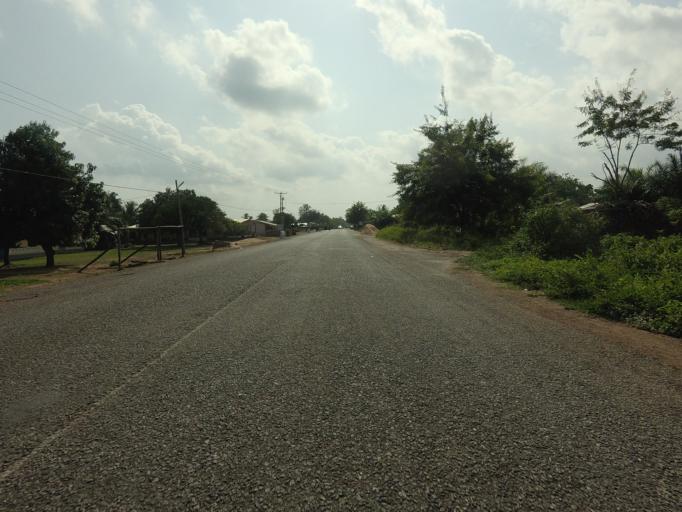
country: GH
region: Volta
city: Ho
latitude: 6.5760
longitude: 0.5881
